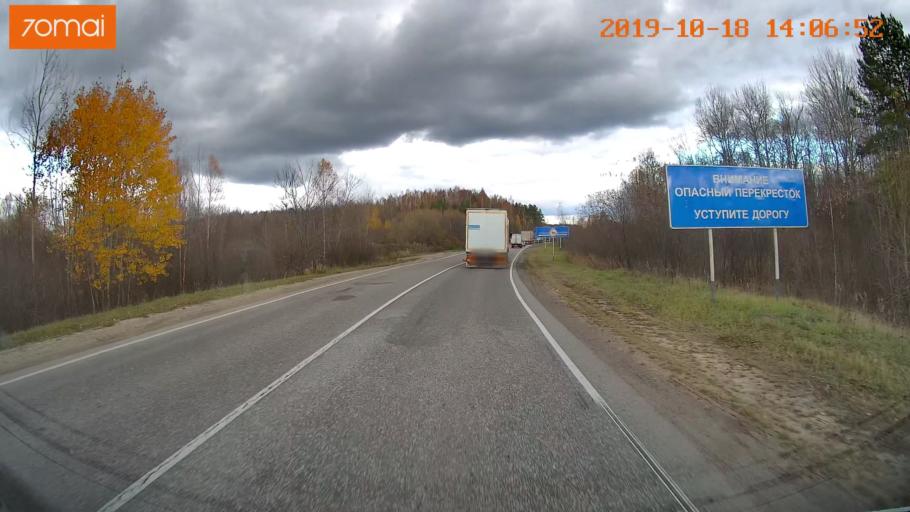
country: RU
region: Rjazan
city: Spas-Klepiki
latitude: 55.1494
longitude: 40.1543
